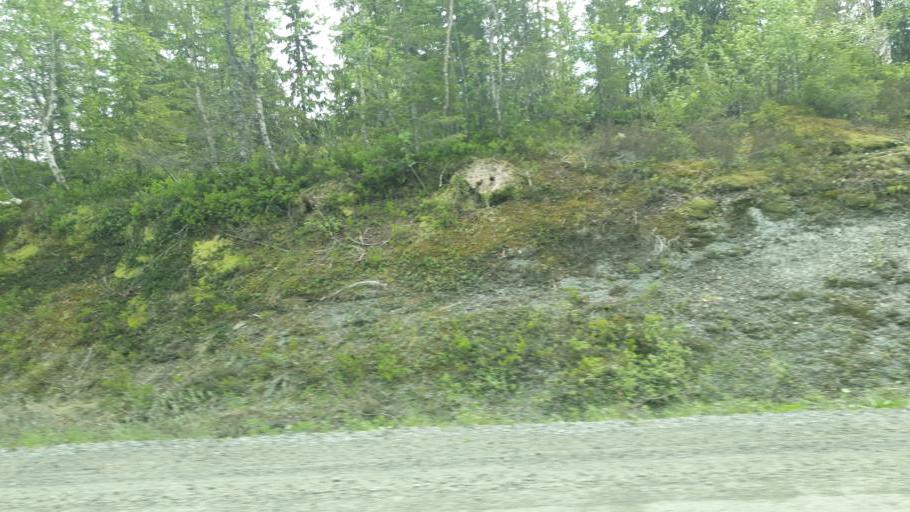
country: NO
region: Sor-Trondelag
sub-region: Trondheim
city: Trondheim
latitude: 63.6793
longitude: 10.3466
